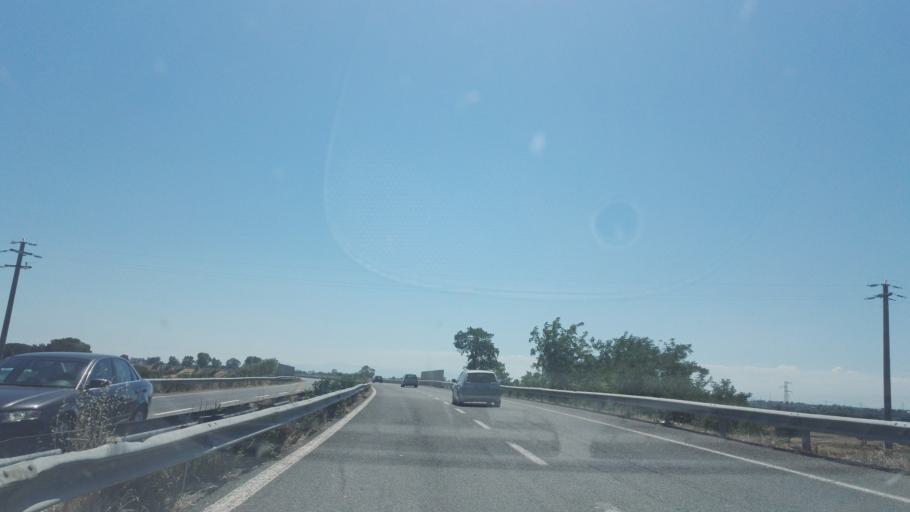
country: IT
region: Apulia
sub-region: Provincia di Taranto
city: Marina di Ginosa
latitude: 40.4296
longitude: 16.8285
